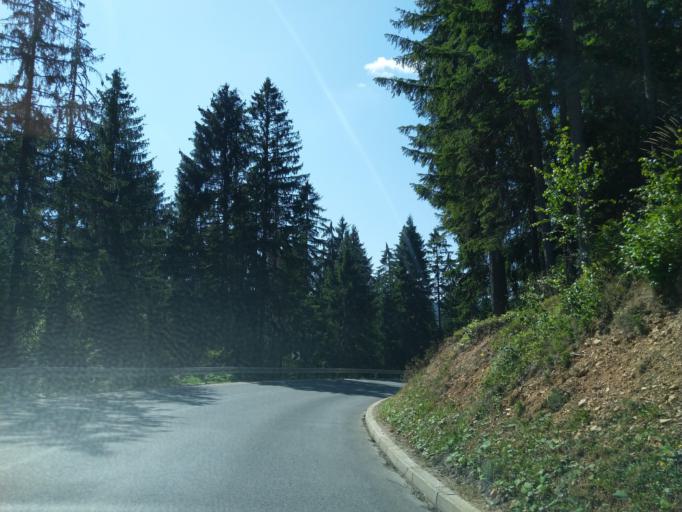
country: RS
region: Central Serbia
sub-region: Zlatiborski Okrug
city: Nova Varos
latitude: 43.4452
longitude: 19.8210
